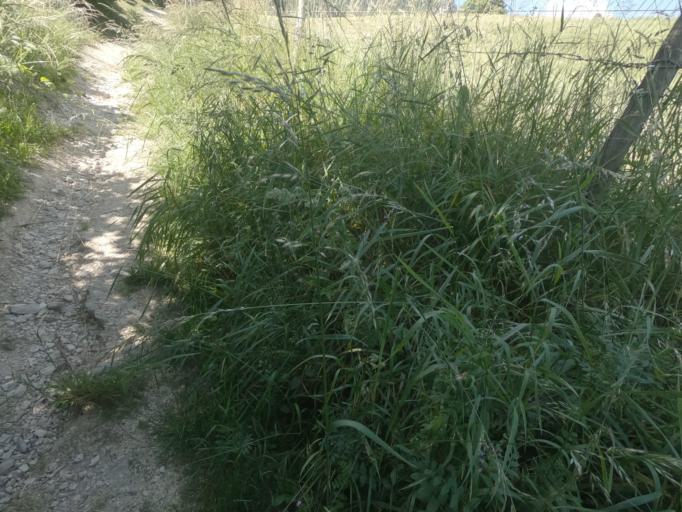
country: CH
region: Solothurn
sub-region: Bezirk Lebern
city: Langendorf
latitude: 47.2361
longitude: 7.5306
